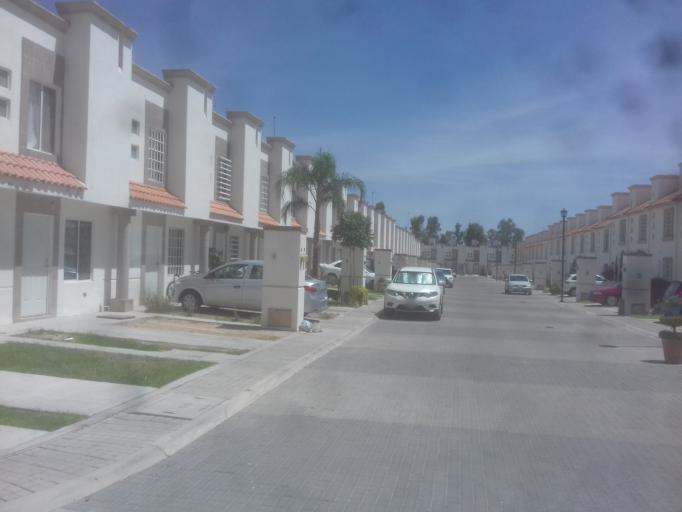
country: MX
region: Aguascalientes
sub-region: Aguascalientes
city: San Sebastian [Fraccionamiento]
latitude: 21.8091
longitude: -102.2967
